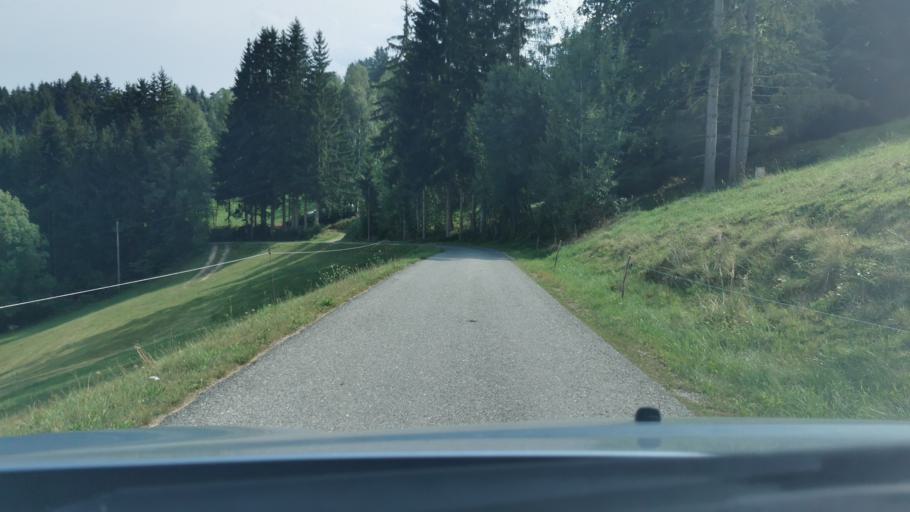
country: AT
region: Styria
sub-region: Politischer Bezirk Weiz
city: Strallegg
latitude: 47.4028
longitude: 15.6947
